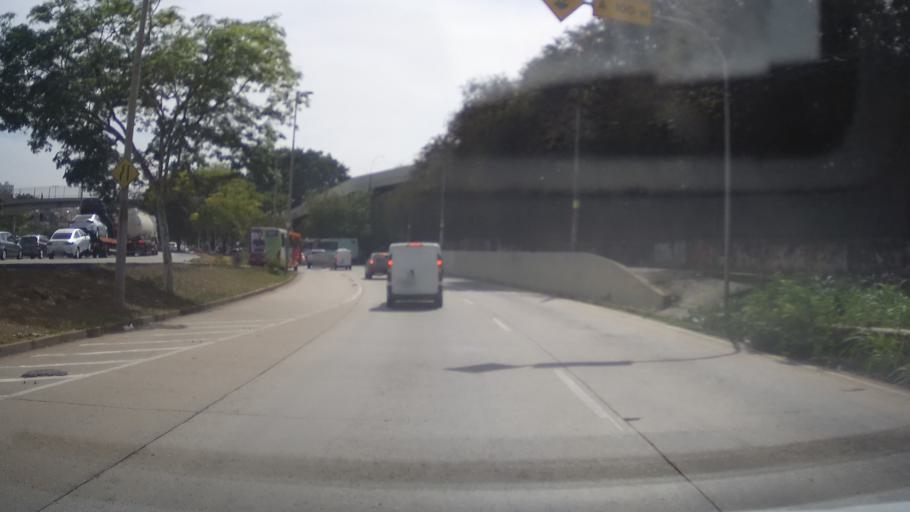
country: BR
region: Minas Gerais
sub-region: Belo Horizonte
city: Belo Horizonte
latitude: -19.9280
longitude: -43.9890
